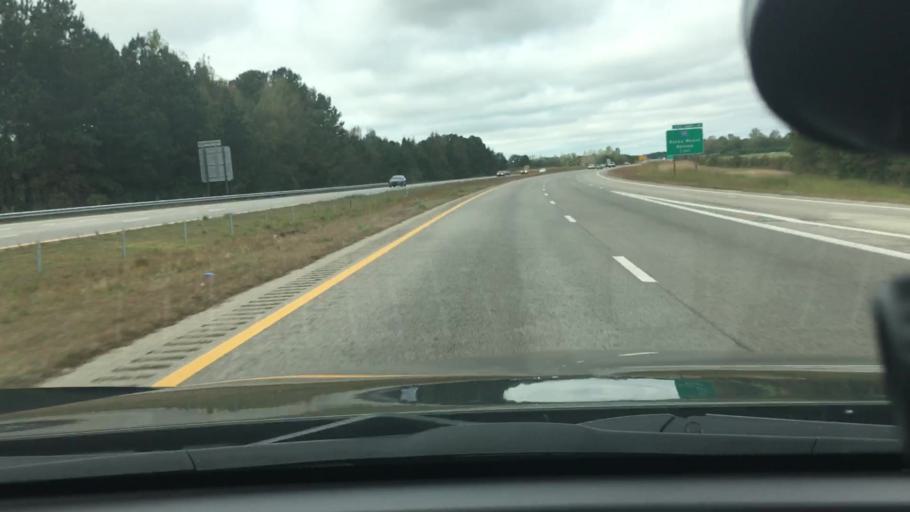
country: US
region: North Carolina
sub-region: Wilson County
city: Lucama
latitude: 35.7149
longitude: -78.0033
